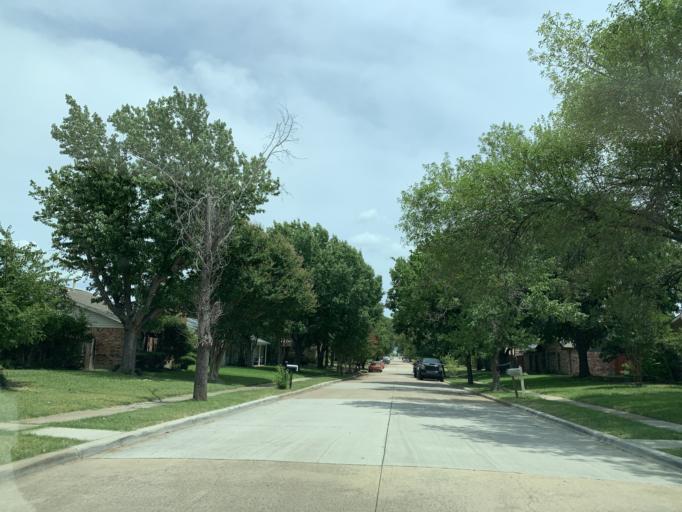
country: US
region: Texas
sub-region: Dallas County
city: Grand Prairie
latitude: 32.6596
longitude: -97.0316
